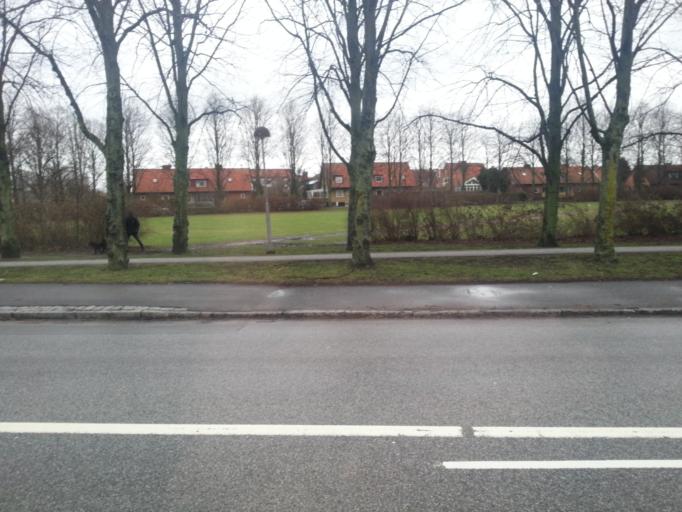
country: SE
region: Skane
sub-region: Lunds Kommun
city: Lund
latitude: 55.7091
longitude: 13.1734
